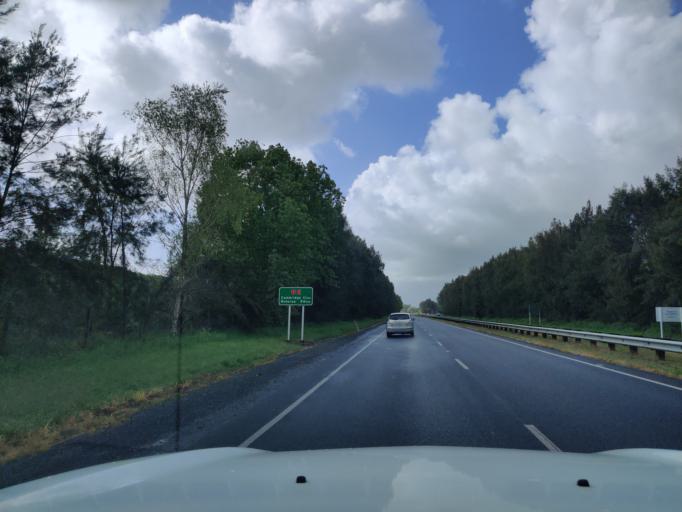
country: NZ
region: Waikato
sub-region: Waipa District
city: Cambridge
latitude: -37.8324
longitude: 175.3617
